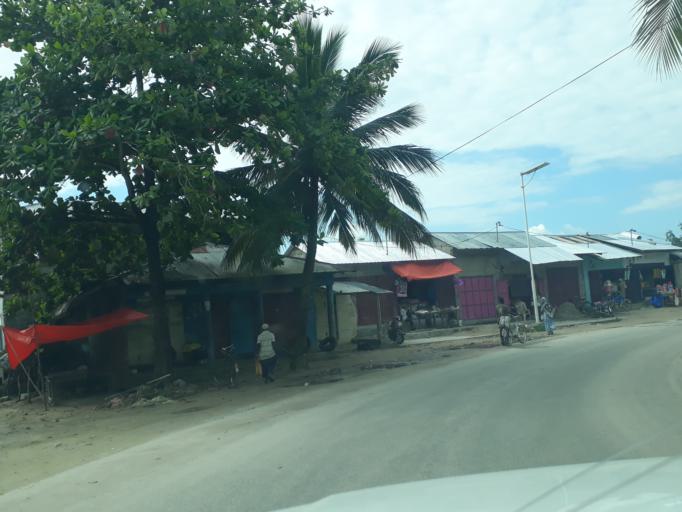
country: TZ
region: Zanzibar North
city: Mkokotoni
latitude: -5.8752
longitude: 39.2552
